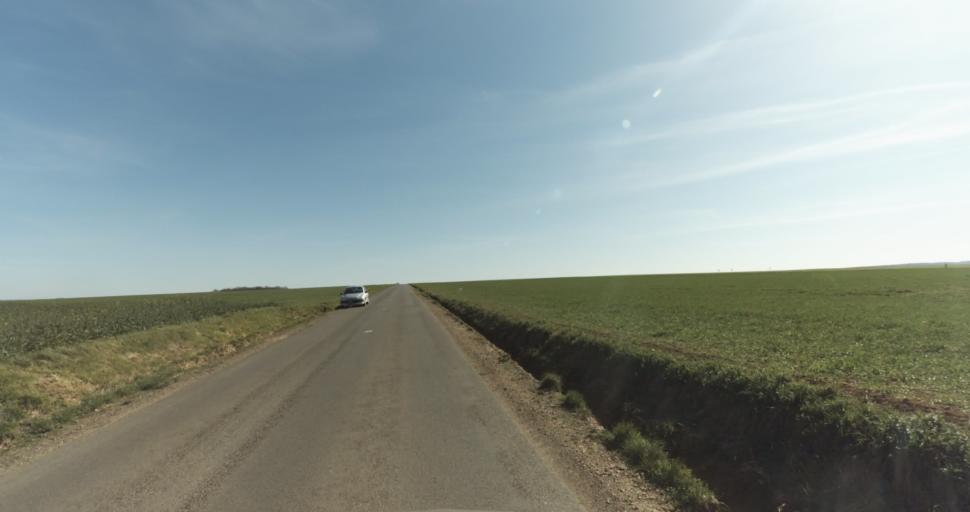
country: FR
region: Lower Normandy
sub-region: Departement du Calvados
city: Saint-Pierre-sur-Dives
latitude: 48.9994
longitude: -0.0475
